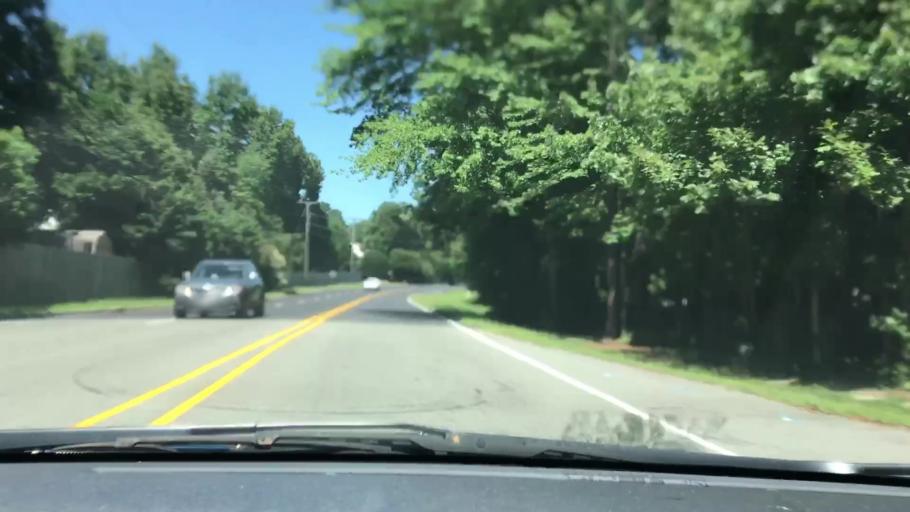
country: US
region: Virginia
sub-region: Henrico County
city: Short Pump
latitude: 37.6379
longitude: -77.6160
